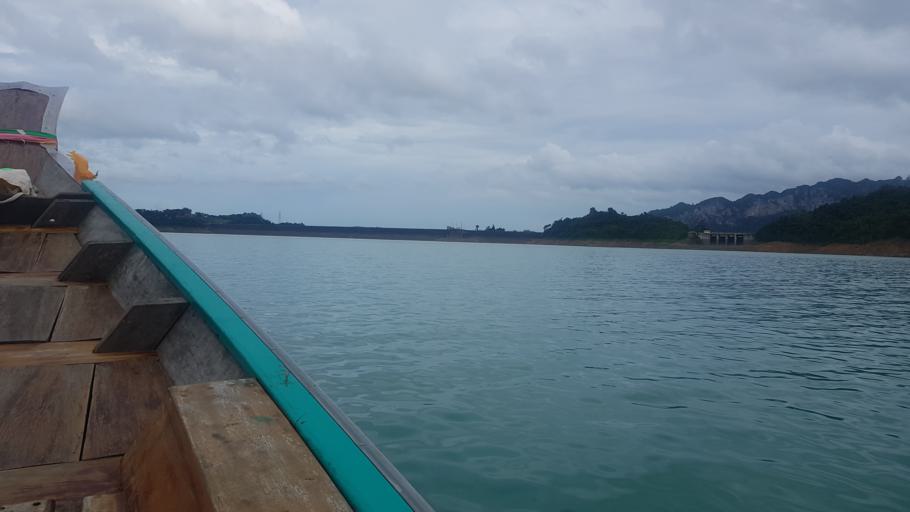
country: TH
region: Surat Thani
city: Ban Takhun
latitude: 8.9812
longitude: 98.7969
